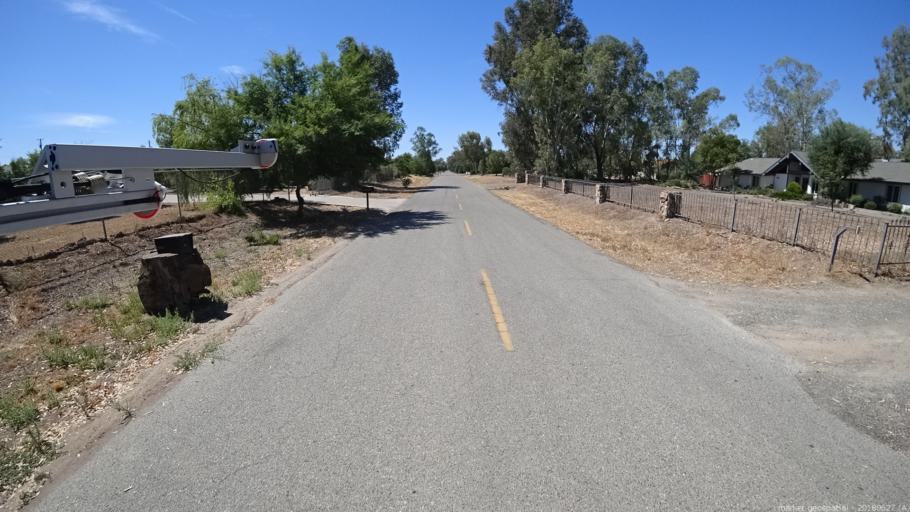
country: US
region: California
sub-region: Madera County
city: Bonadelle Ranchos-Madera Ranchos
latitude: 36.9357
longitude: -119.8823
